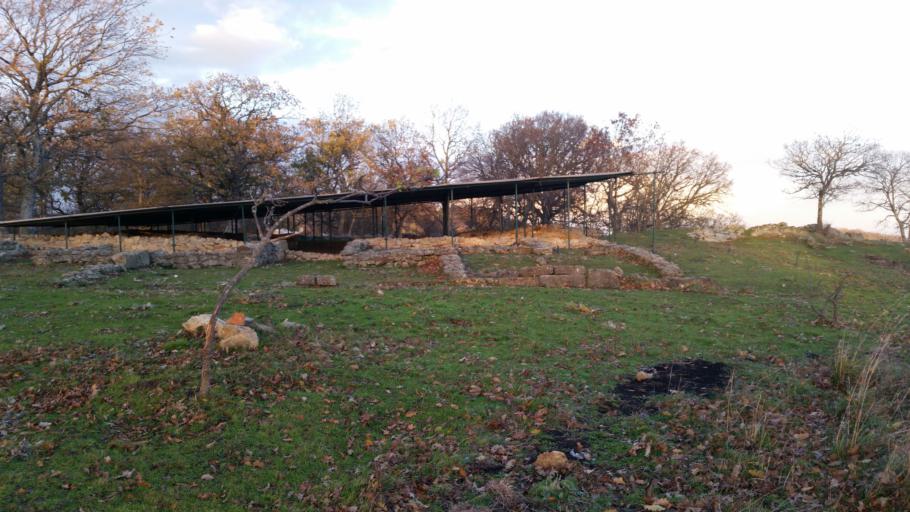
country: IT
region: Basilicate
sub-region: Provincia di Potenza
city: San Chirico Nuovo
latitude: 40.6375
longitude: 16.0588
